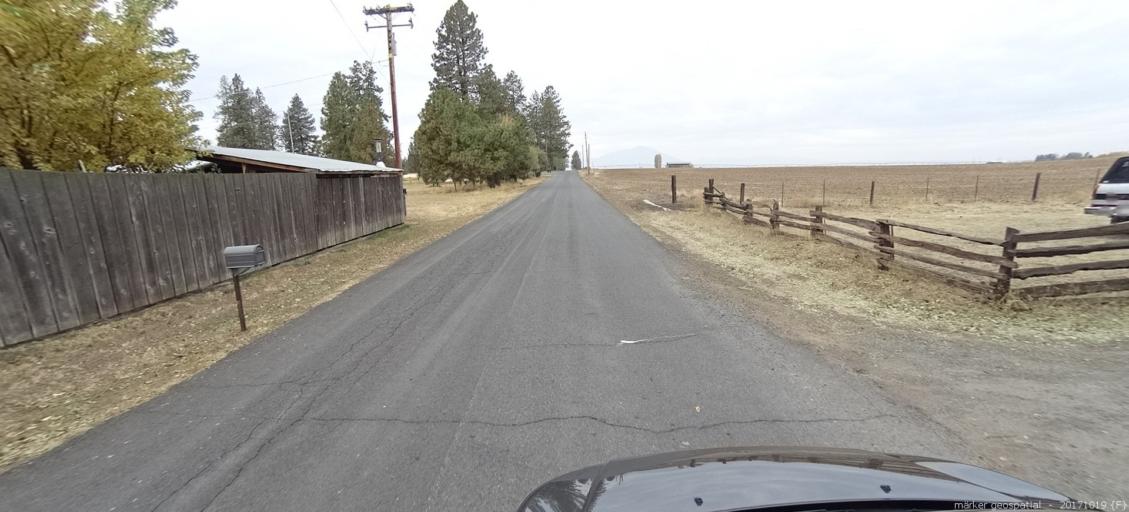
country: US
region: California
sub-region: Shasta County
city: Burney
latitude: 41.0585
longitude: -121.3792
